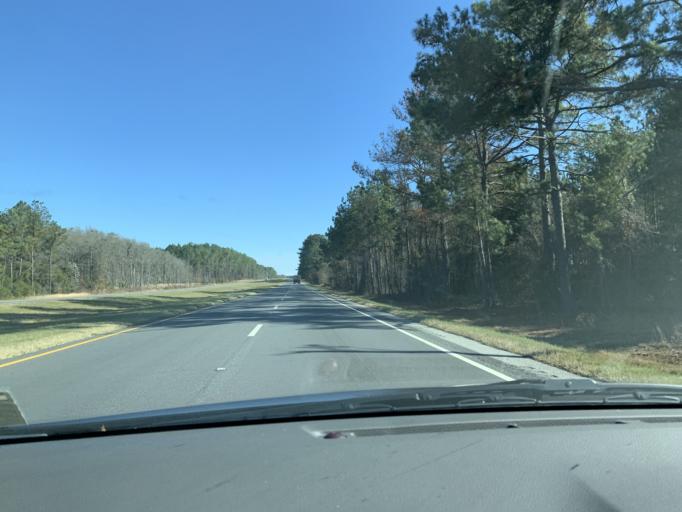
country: US
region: Georgia
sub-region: Atkinson County
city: Willacoochee
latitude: 31.3312
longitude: -83.0143
